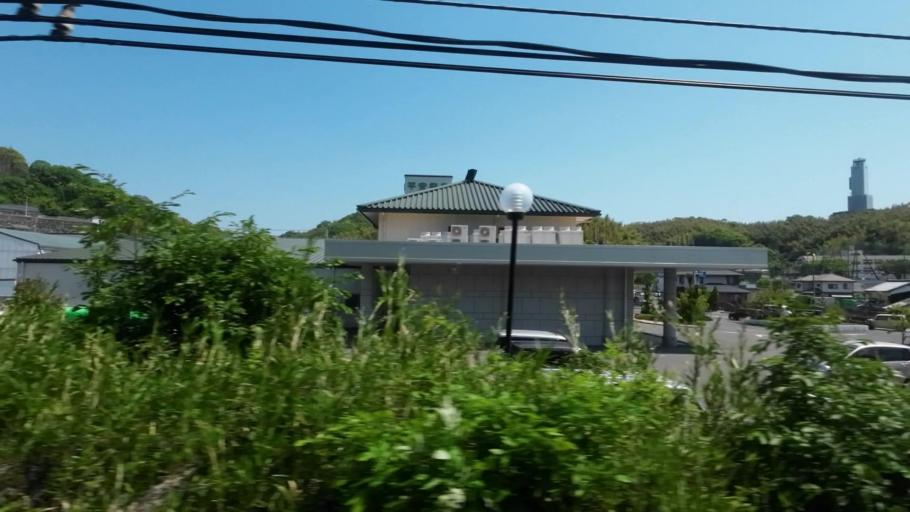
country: JP
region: Ehime
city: Hojo
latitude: 34.0894
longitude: 132.9824
